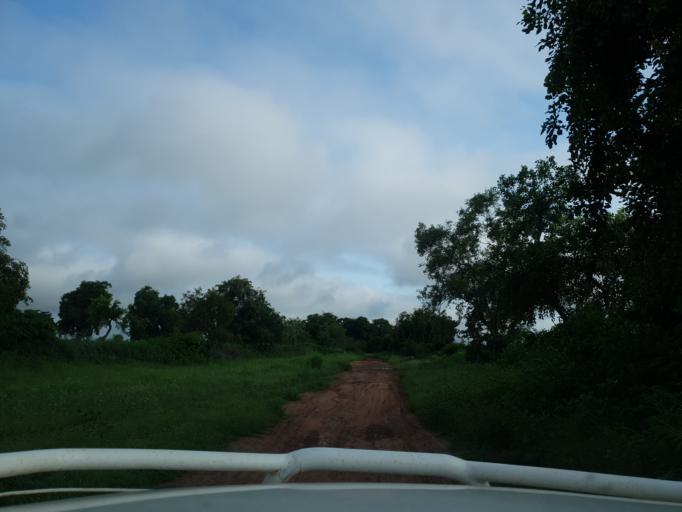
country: ML
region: Segou
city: Baroueli
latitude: 13.3970
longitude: -7.0052
